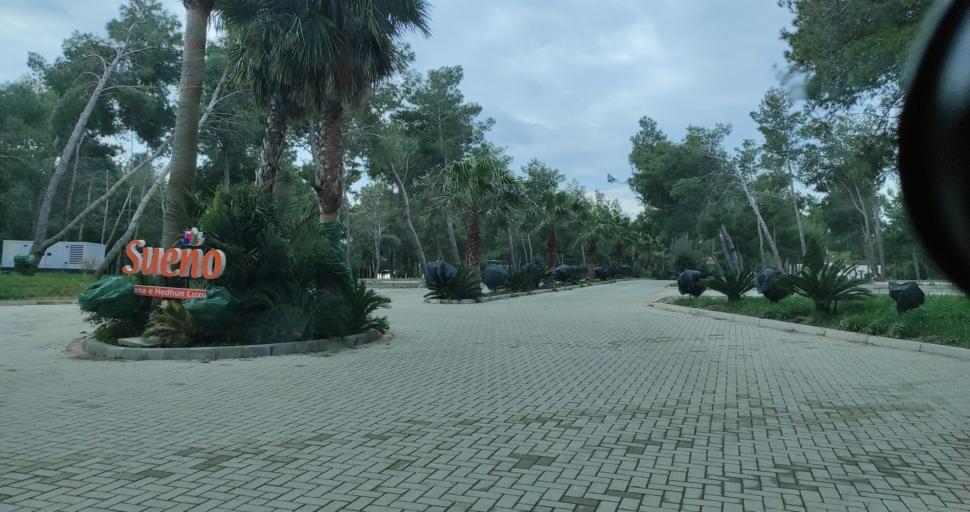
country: AL
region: Lezhe
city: Shengjin
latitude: 41.8225
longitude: 19.5614
